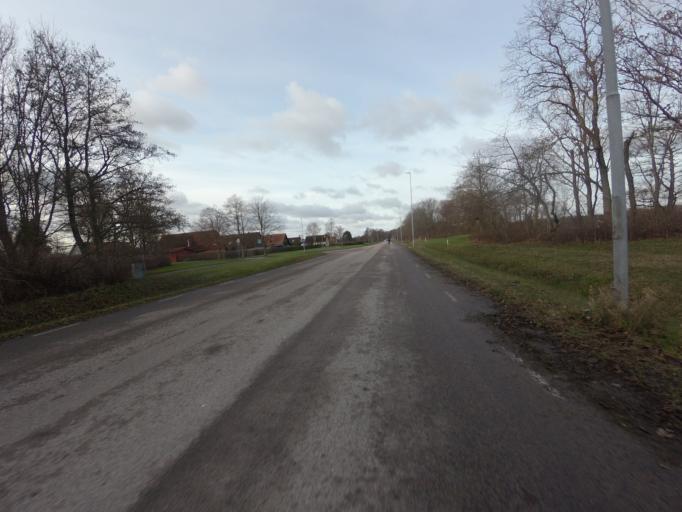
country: SE
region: Skane
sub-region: Hoganas Kommun
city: Hoganas
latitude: 56.1819
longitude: 12.5723
